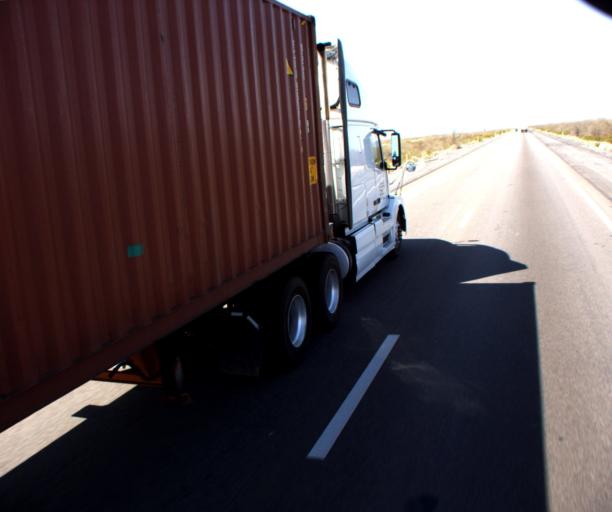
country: US
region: Arizona
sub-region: La Paz County
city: Salome
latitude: 33.5907
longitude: -113.4950
